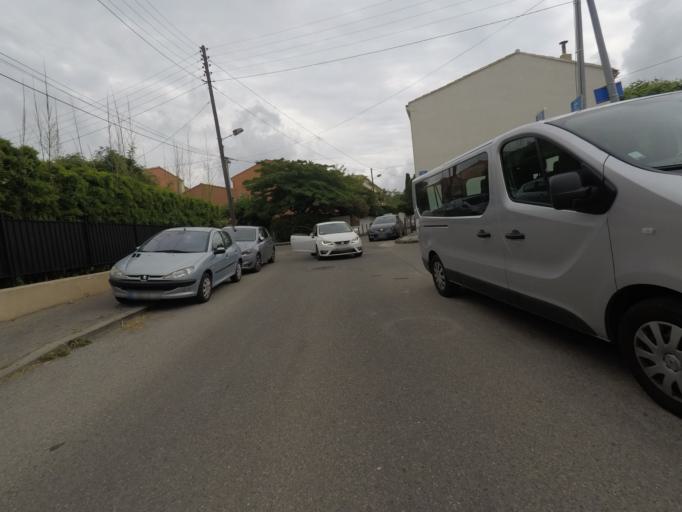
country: FR
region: Provence-Alpes-Cote d'Azur
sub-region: Departement des Bouches-du-Rhone
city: Marseille 08
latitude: 43.2636
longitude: 5.3914
